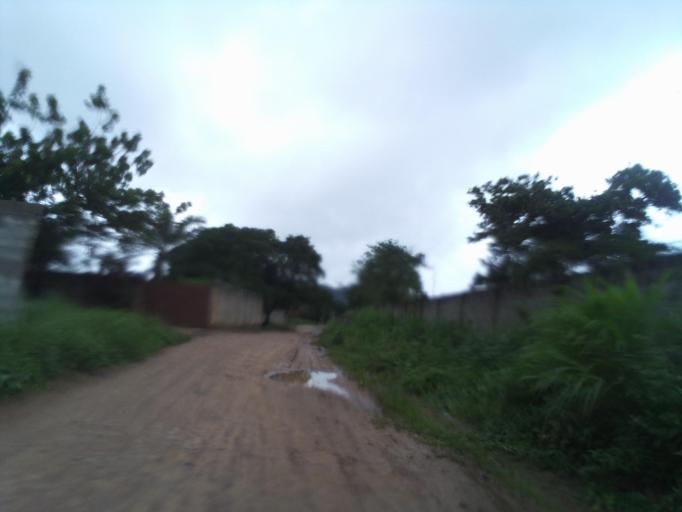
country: SL
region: Eastern Province
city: Kenema
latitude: 7.8539
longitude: -11.2073
